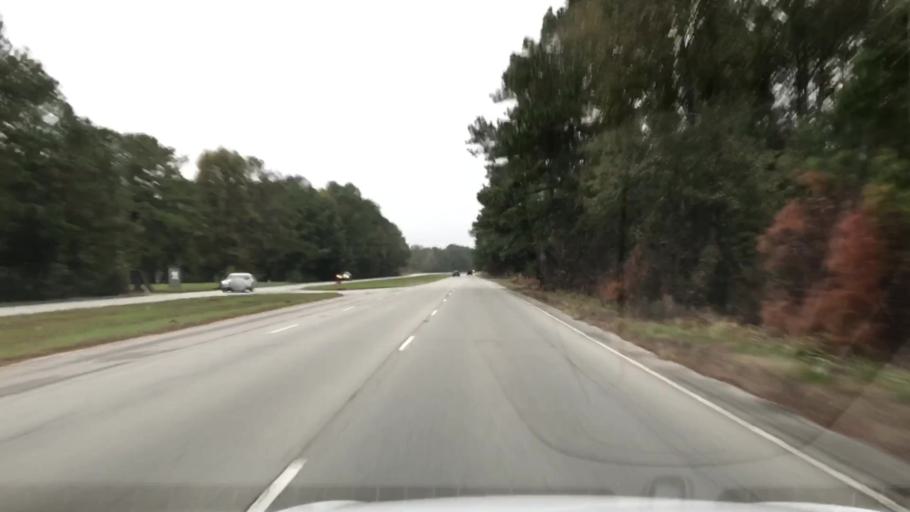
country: US
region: South Carolina
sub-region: Charleston County
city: Awendaw
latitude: 32.9973
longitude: -79.6444
